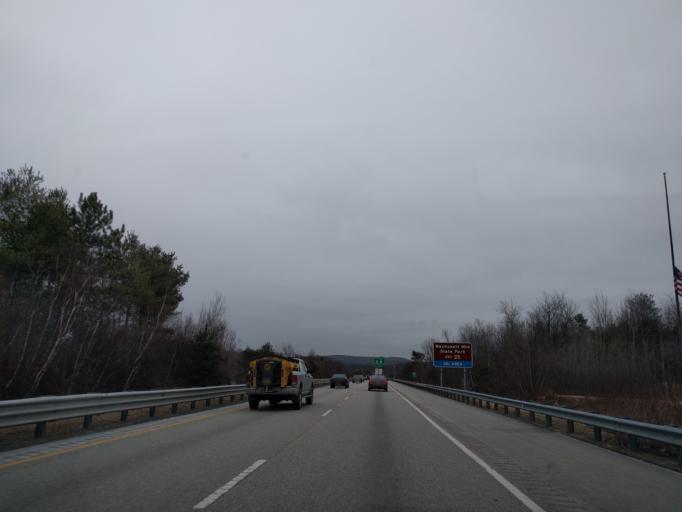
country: US
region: Massachusetts
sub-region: Worcester County
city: Westminster
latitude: 42.5519
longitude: -71.9150
